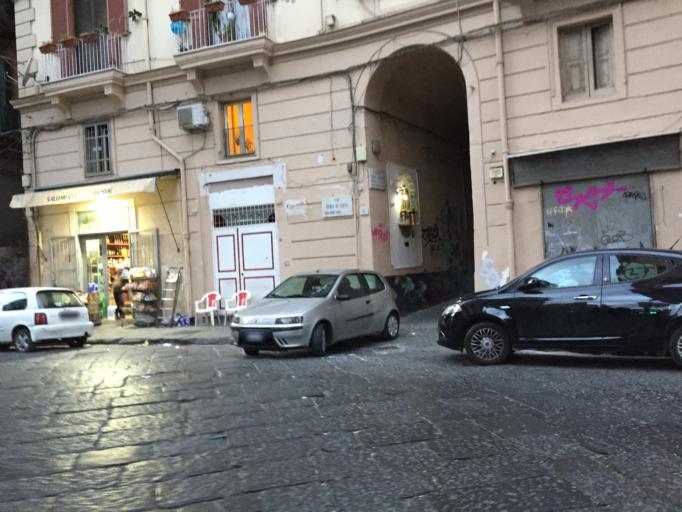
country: IT
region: Campania
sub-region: Provincia di Napoli
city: Napoli
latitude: 40.8443
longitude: 14.2549
